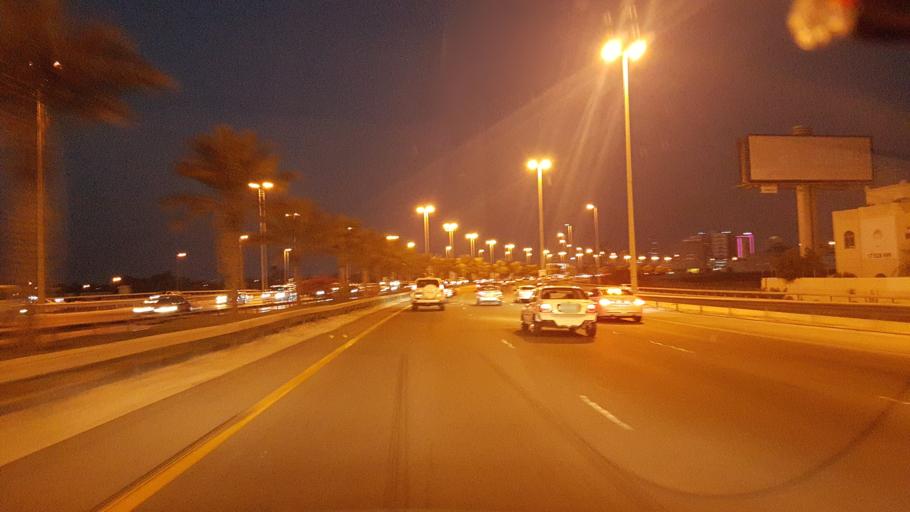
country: BH
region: Manama
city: Jidd Hafs
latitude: 26.2214
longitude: 50.5222
